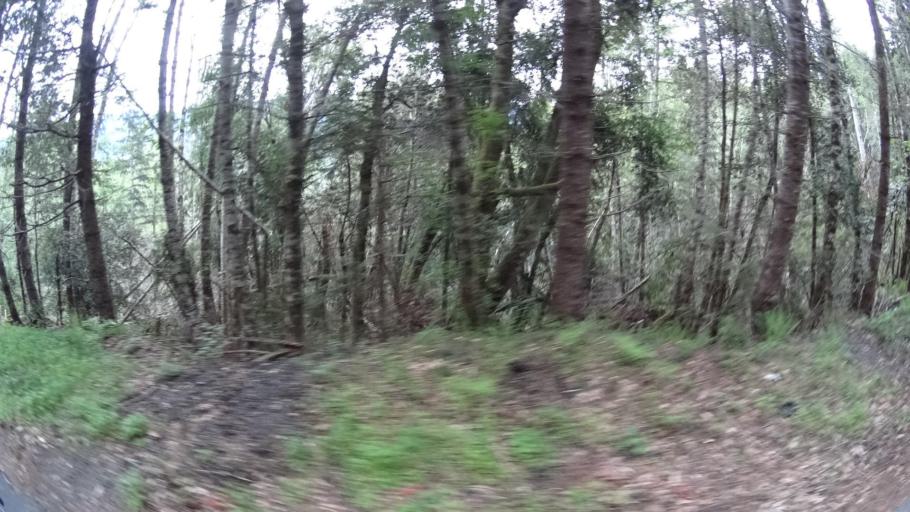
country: US
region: California
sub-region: Humboldt County
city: Blue Lake
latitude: 40.9336
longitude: -123.8491
